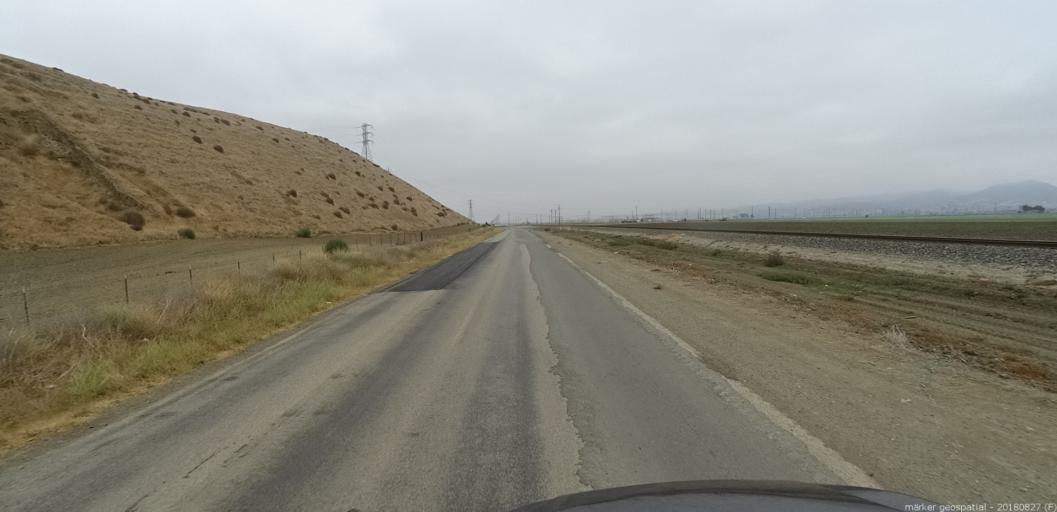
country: US
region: California
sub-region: Monterey County
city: King City
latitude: 36.2719
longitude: -121.1457
